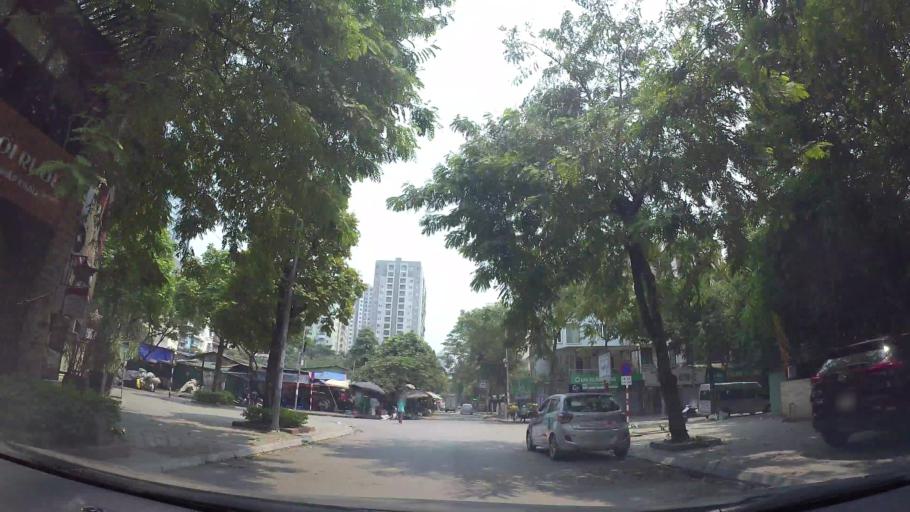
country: VN
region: Ha Noi
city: Thanh Xuan
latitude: 21.0059
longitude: 105.8009
